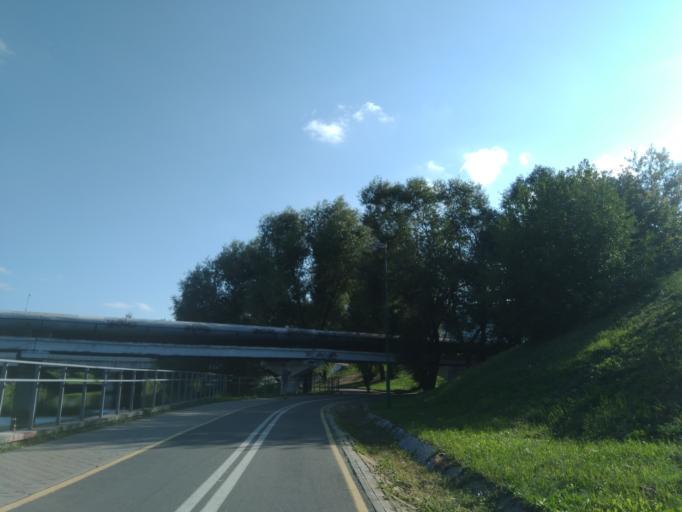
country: BY
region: Minsk
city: Minsk
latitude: 53.8876
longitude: 27.5714
